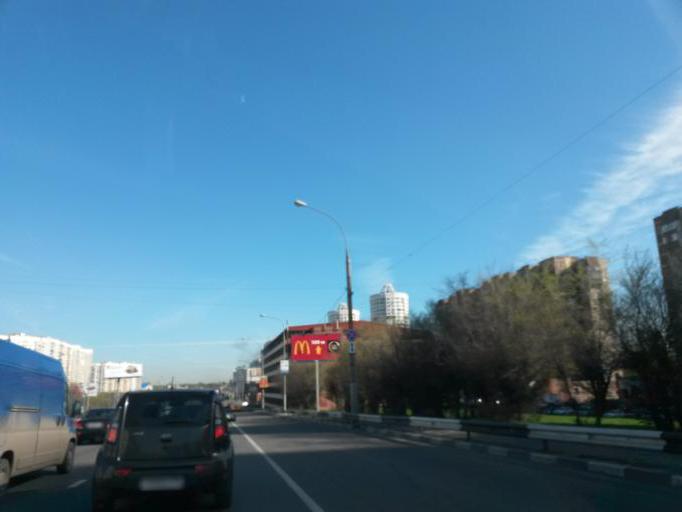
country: RU
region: Moscow
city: Brateyevo
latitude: 55.6451
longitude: 37.7459
